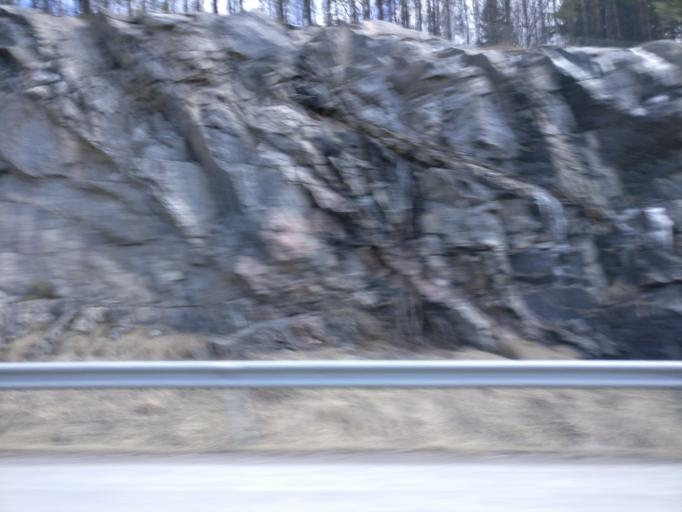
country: FI
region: Haeme
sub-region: Riihimaeki
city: Riihimaeki
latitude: 60.7454
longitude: 24.7298
